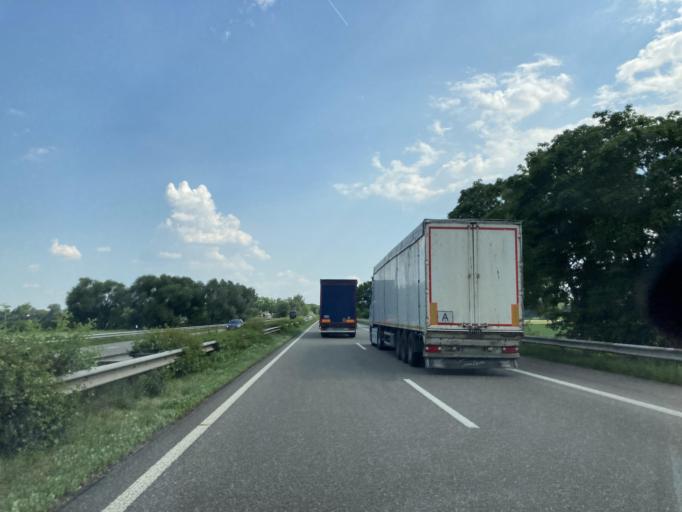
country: DE
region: Rheinland-Pfalz
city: Kuhardt
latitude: 49.1359
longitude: 8.3059
